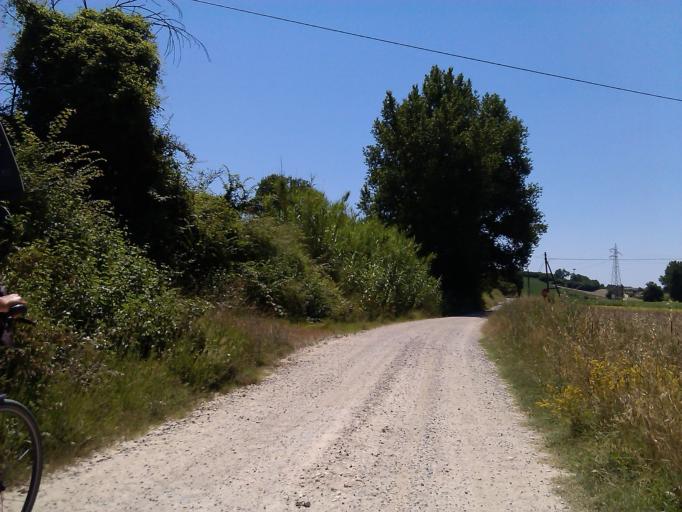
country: IT
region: Umbria
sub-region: Provincia di Terni
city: Ficulle
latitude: 42.8465
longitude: 12.0419
